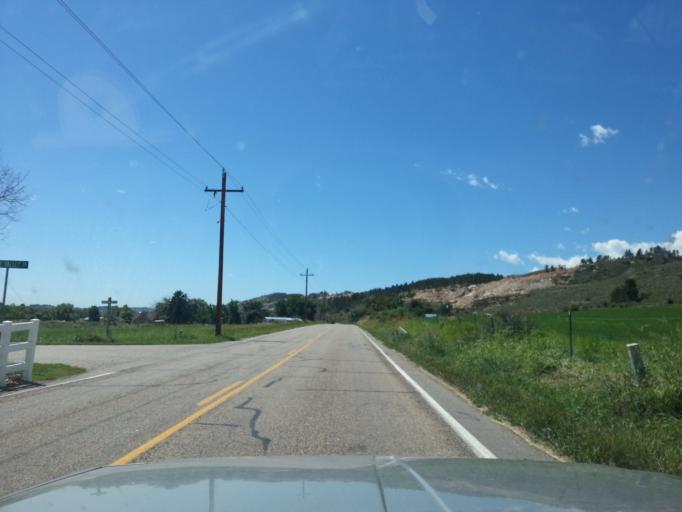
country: US
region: Colorado
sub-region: Larimer County
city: Loveland
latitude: 40.4621
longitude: -105.2067
